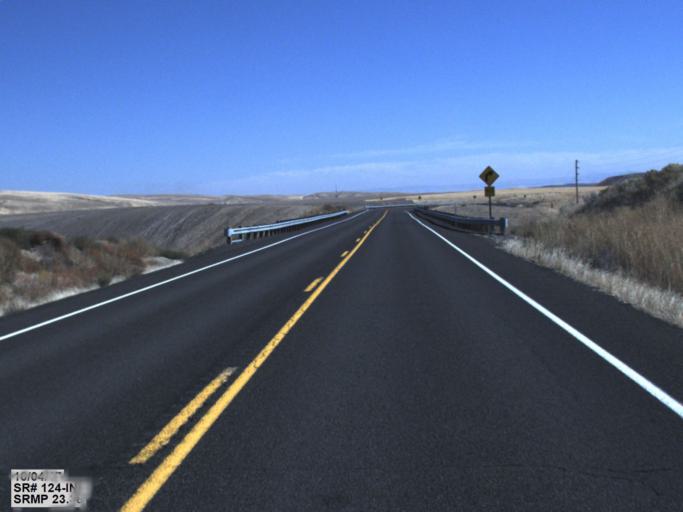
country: US
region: Washington
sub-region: Walla Walla County
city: Garrett
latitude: 46.2964
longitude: -118.5676
